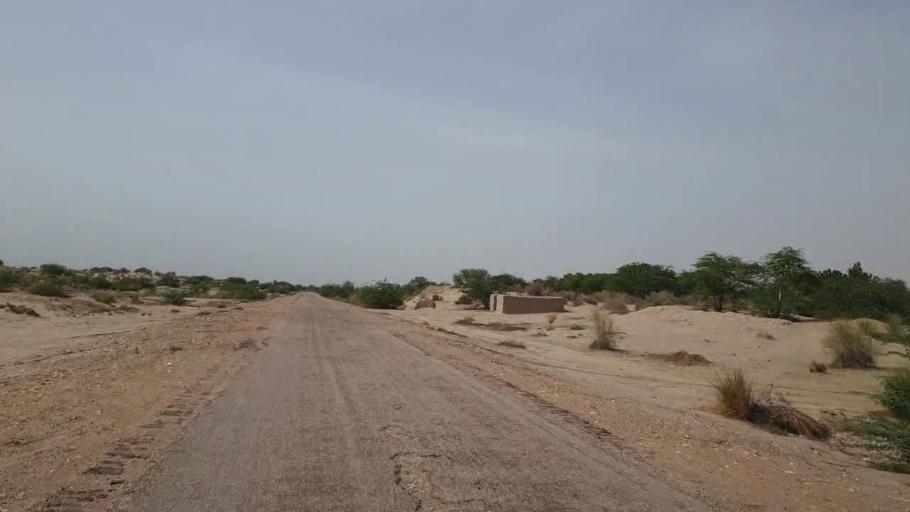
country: PK
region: Sindh
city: Bandhi
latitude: 26.5453
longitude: 68.3854
